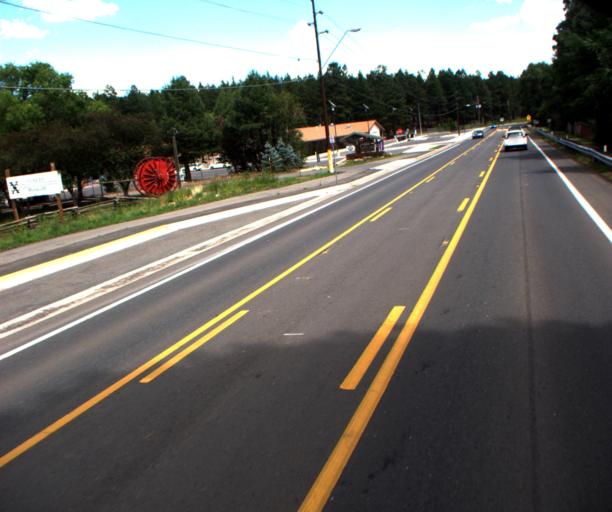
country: US
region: Arizona
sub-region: Coconino County
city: Flagstaff
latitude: 35.2232
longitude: -111.6554
